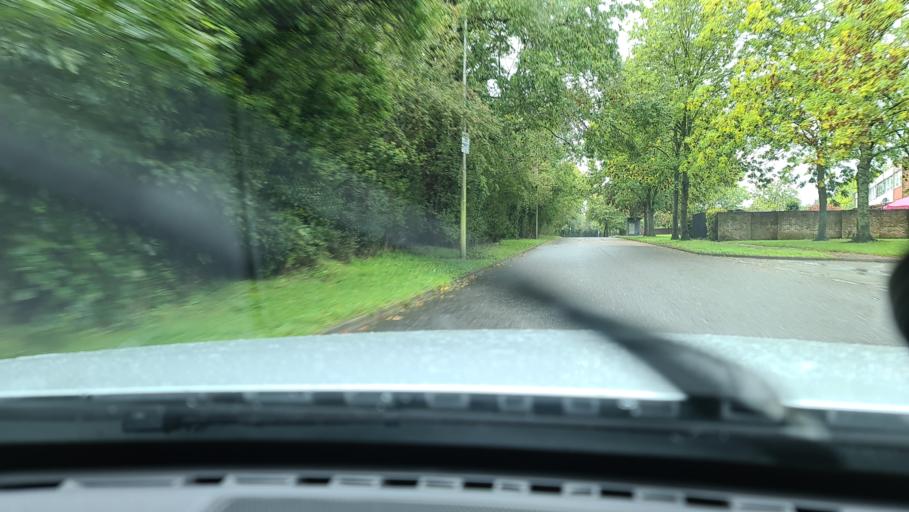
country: GB
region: England
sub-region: Milton Keynes
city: Water Eaton
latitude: 51.9766
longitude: -0.7188
